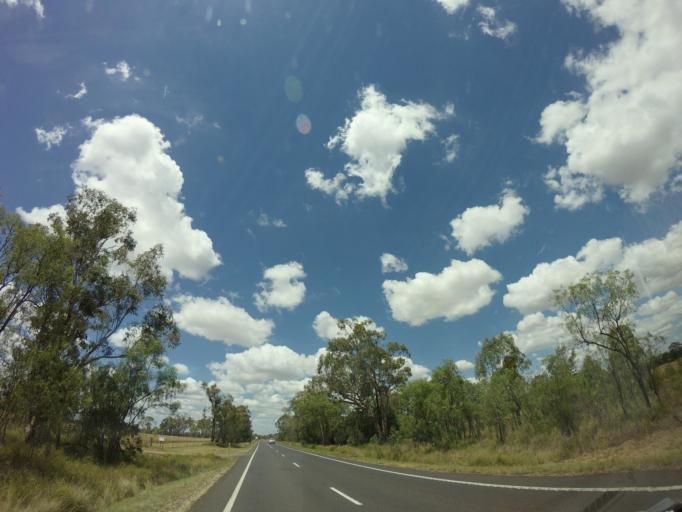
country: AU
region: Queensland
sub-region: Toowoomba
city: Oakey
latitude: -27.8875
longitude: 151.2190
